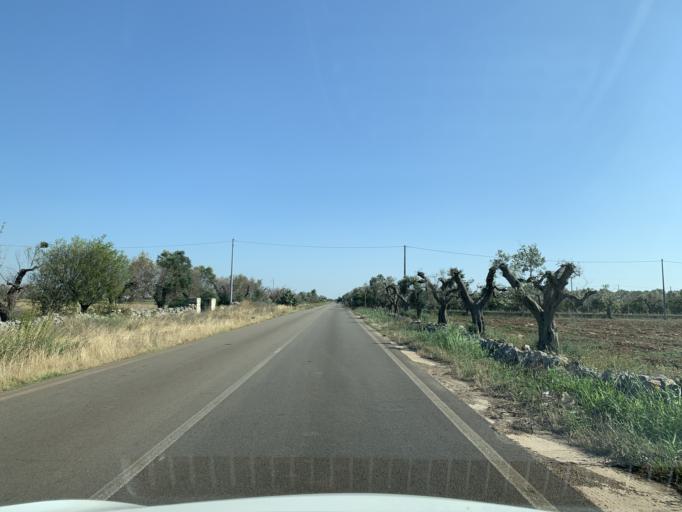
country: IT
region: Apulia
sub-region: Provincia di Lecce
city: Copertino
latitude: 40.2564
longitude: 18.0207
